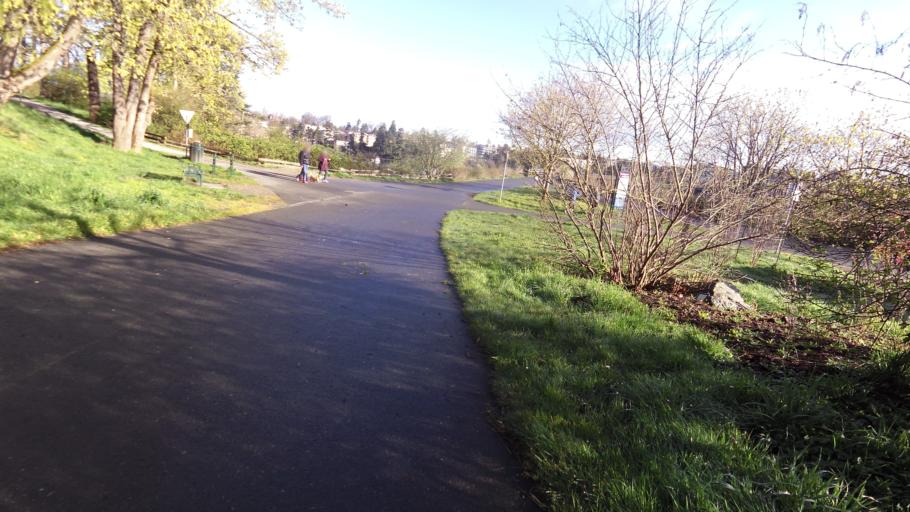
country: CA
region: British Columbia
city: Victoria
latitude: 48.4377
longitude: -123.3832
